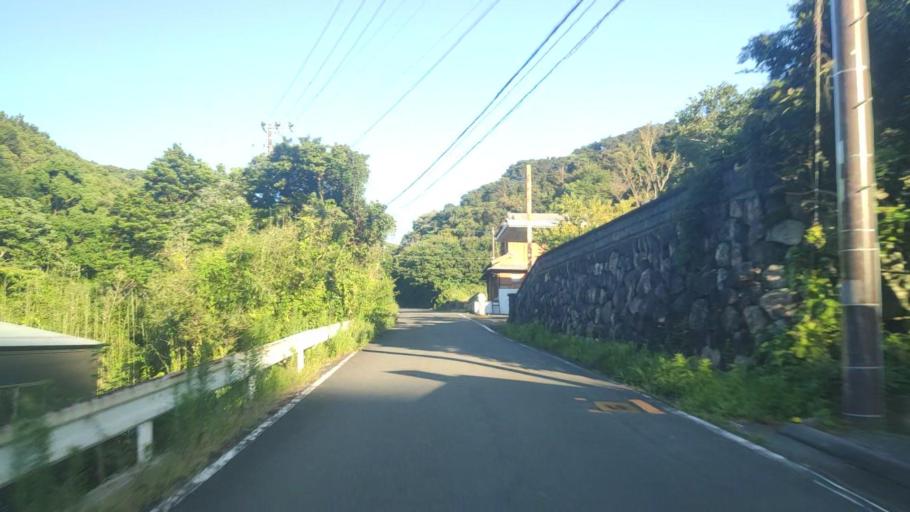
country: JP
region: Mie
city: Ise
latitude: 34.2698
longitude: 136.7669
